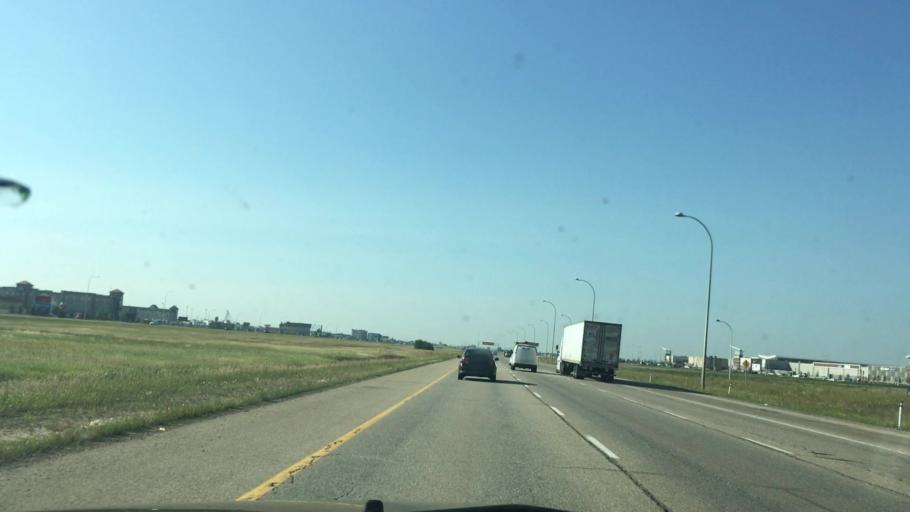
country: CA
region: Alberta
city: Leduc
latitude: 53.3079
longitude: -113.5499
